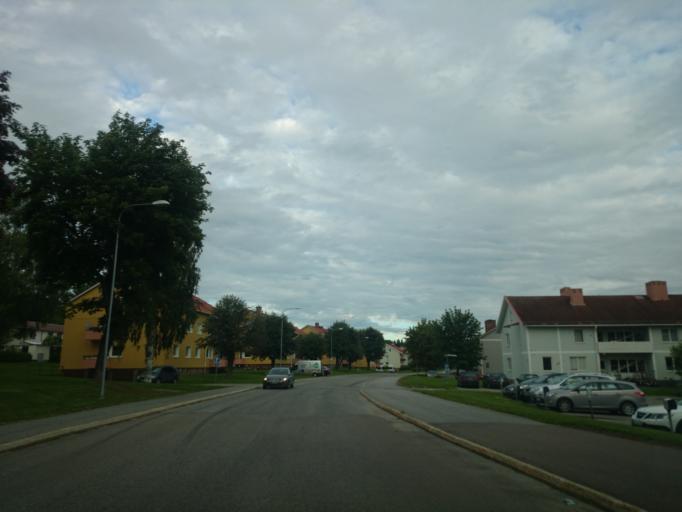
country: SE
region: Vaesternorrland
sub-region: Sundsvalls Kommun
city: Sundsvall
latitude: 62.4051
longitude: 17.2596
